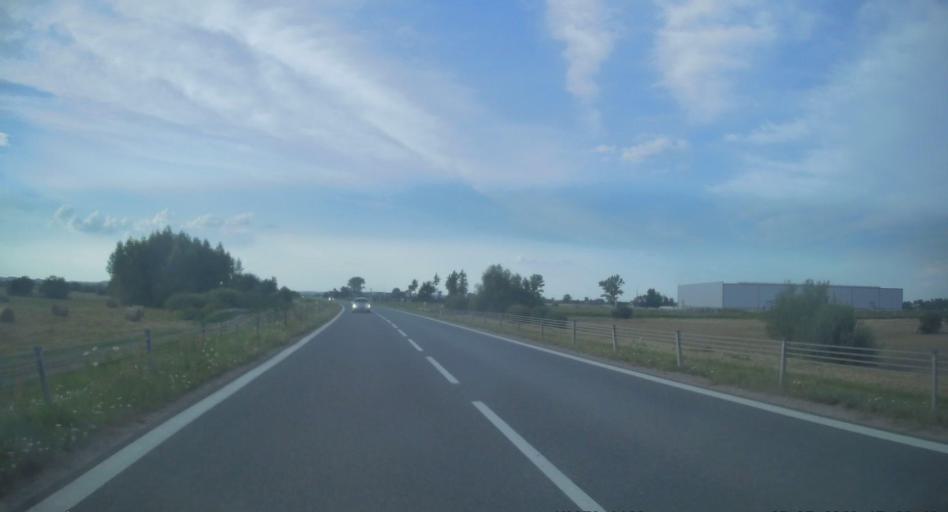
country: PL
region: Lesser Poland Voivodeship
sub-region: Powiat brzeski
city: Szczurowa
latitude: 50.1084
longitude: 20.6192
